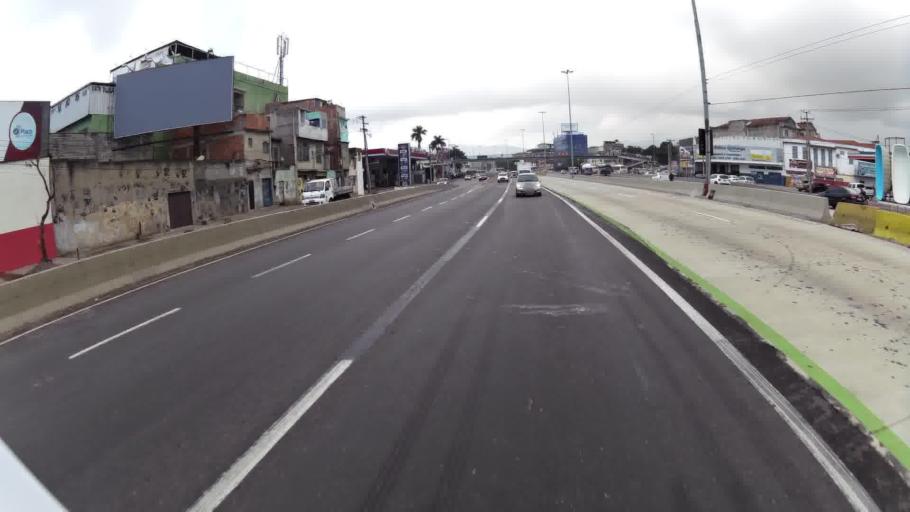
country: BR
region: Rio de Janeiro
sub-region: Rio De Janeiro
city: Rio de Janeiro
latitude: -22.8627
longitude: -43.2478
